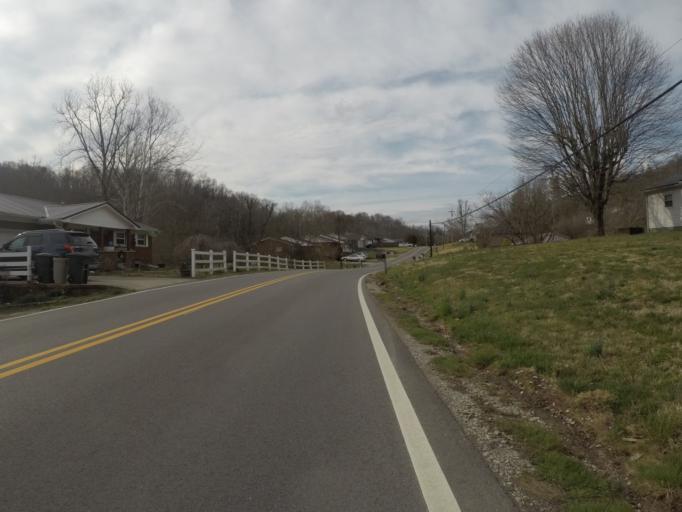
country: US
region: Ohio
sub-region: Lawrence County
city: Burlington
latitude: 38.4368
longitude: -82.4962
